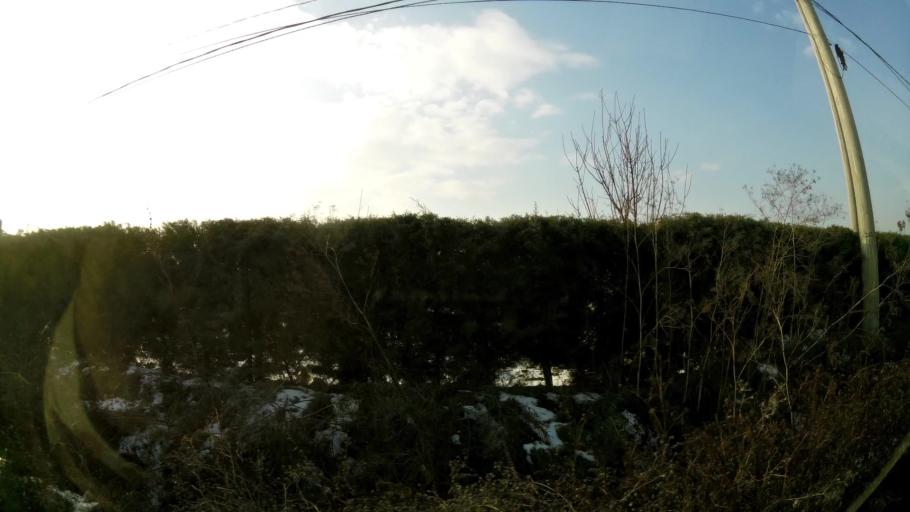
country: MK
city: Creshevo
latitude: 42.0211
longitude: 21.5093
